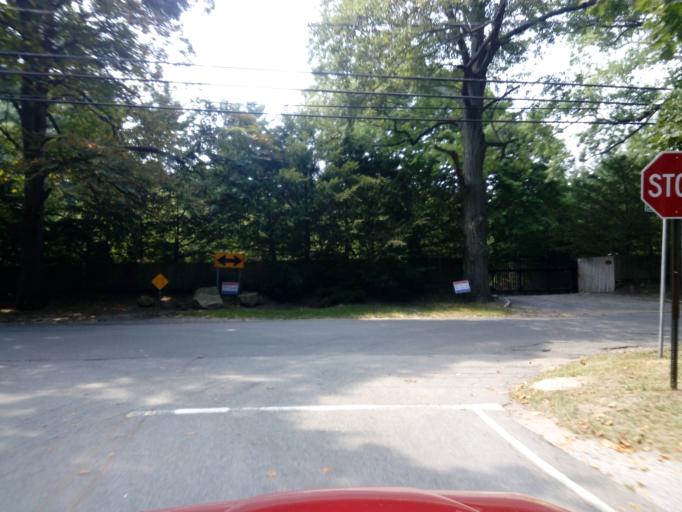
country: US
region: New York
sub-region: Nassau County
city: Glen Cove
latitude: 40.8782
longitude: -73.6413
